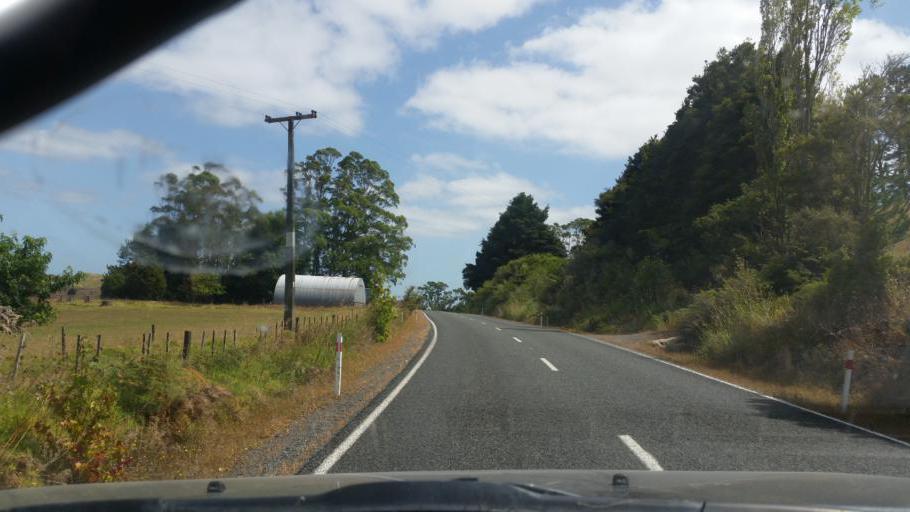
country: NZ
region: Northland
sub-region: Whangarei
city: Ruakaka
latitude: -35.9472
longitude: 174.2931
